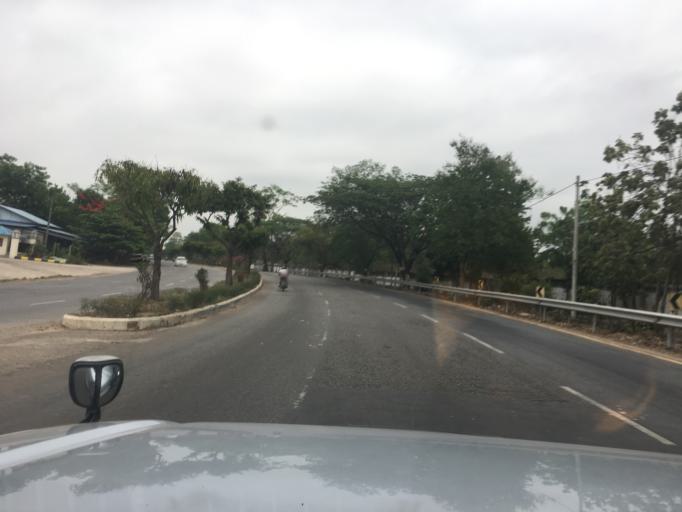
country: MM
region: Bago
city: Thanatpin
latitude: 17.1930
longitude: 96.3993
